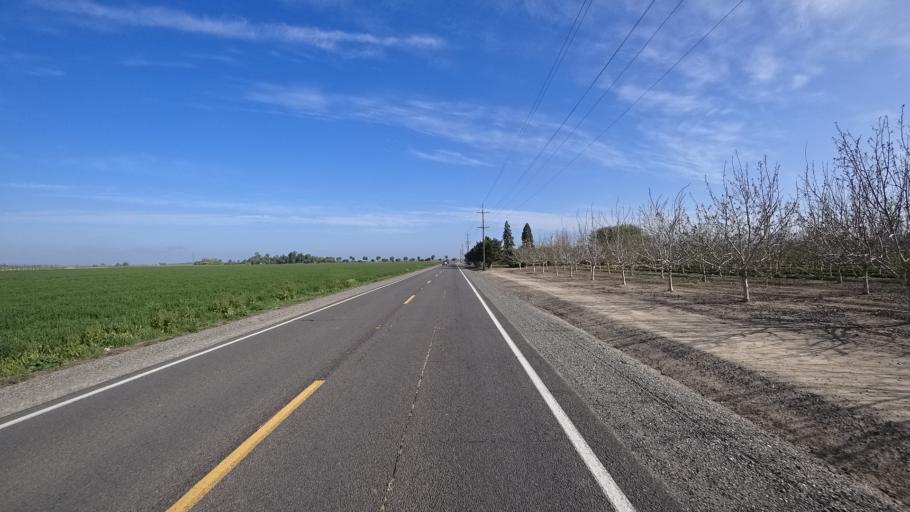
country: US
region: California
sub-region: Glenn County
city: Hamilton City
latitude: 39.5994
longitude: -122.0077
